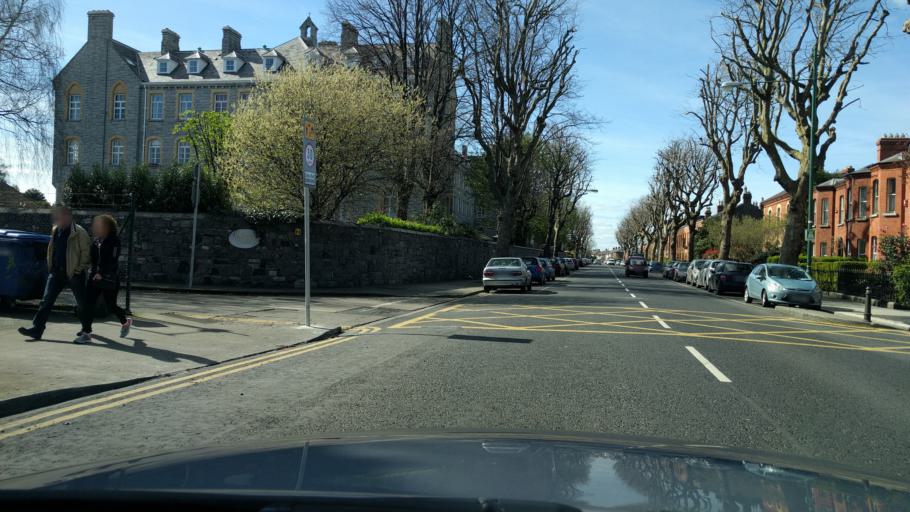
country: IE
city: Greenhills
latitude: 53.3390
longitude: -6.3035
